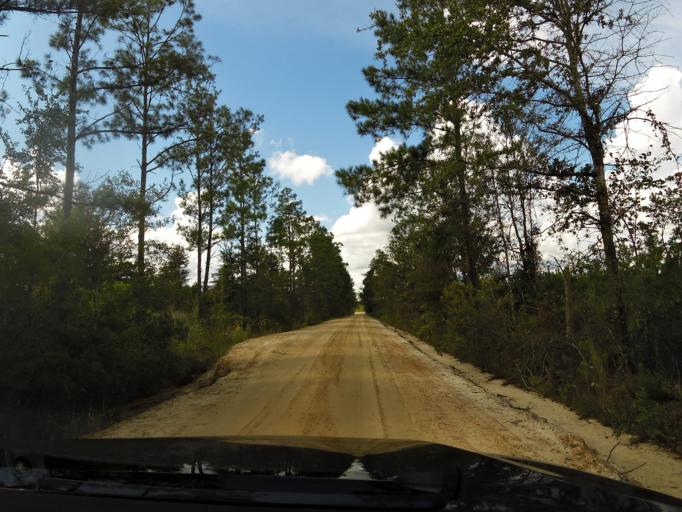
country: US
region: Georgia
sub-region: Brantley County
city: Nahunta
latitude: 31.0917
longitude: -82.0221
